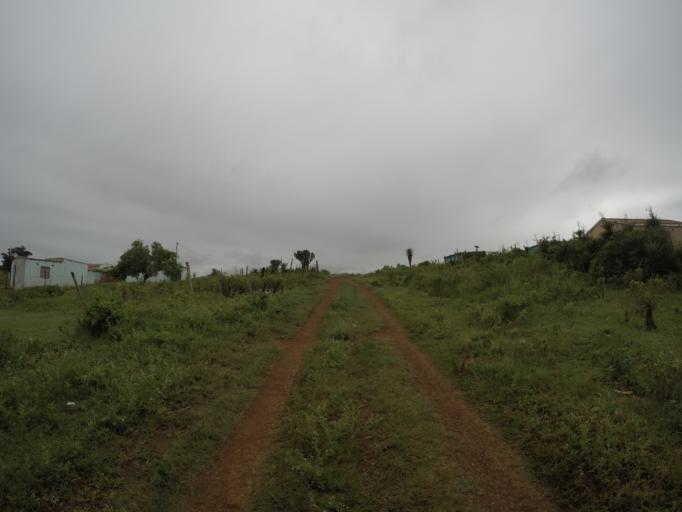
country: ZA
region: KwaZulu-Natal
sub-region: uThungulu District Municipality
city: Empangeni
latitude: -28.6041
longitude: 31.8445
